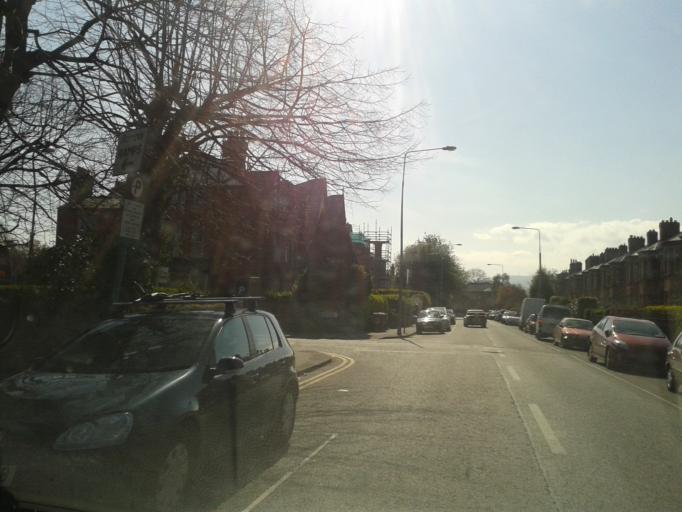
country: IE
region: Leinster
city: Rathmines
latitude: 53.3153
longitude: -6.2648
